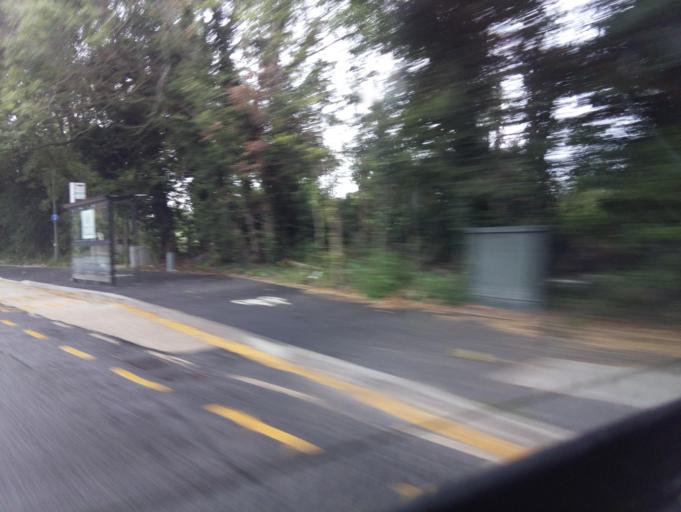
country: GB
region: England
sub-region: Surrey
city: Horley
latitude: 51.1862
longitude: -0.1638
